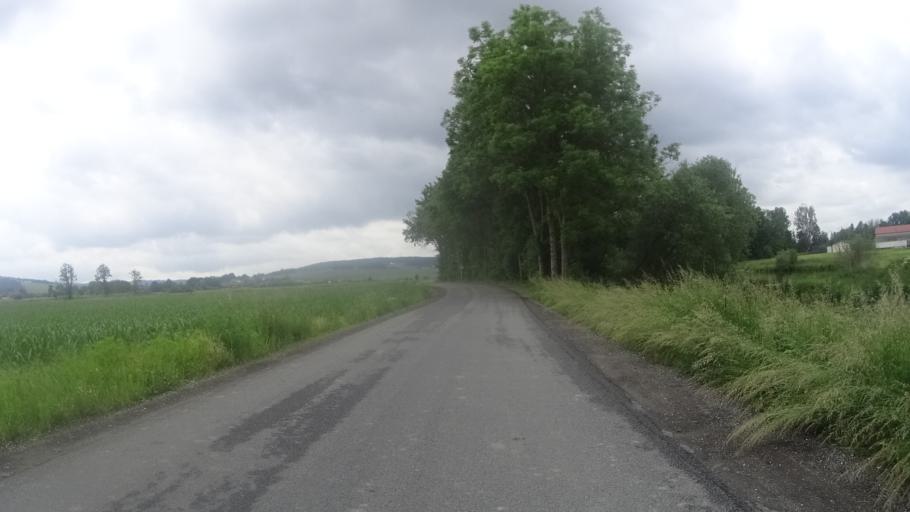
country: DE
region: Bavaria
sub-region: Lower Bavaria
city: Triftern
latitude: 48.4424
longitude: 13.0172
